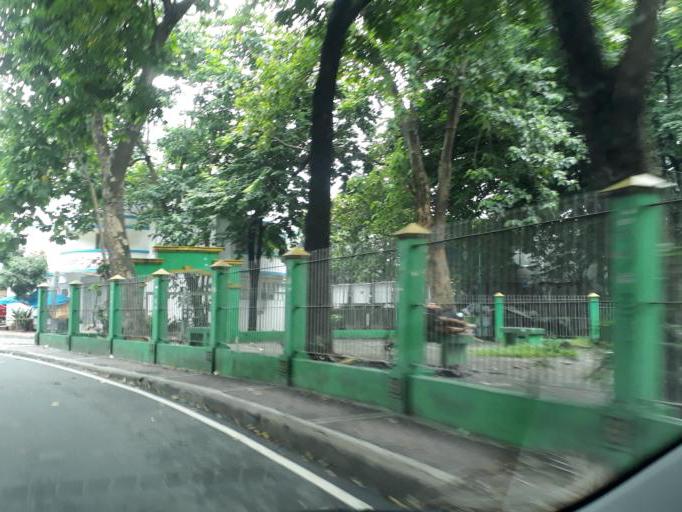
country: PH
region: Calabarzon
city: Del Monte
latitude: 14.6314
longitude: 121.0213
